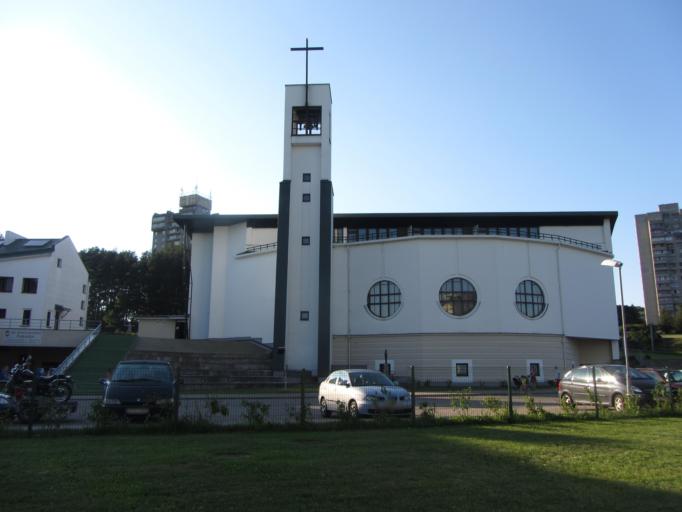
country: LT
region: Vilnius County
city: Lazdynai
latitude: 54.6784
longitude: 25.2113
